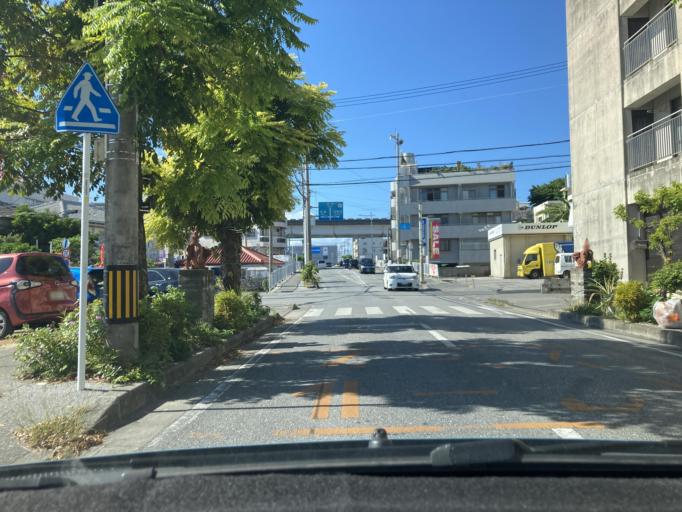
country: JP
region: Okinawa
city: Naha-shi
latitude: 26.2423
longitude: 127.6930
